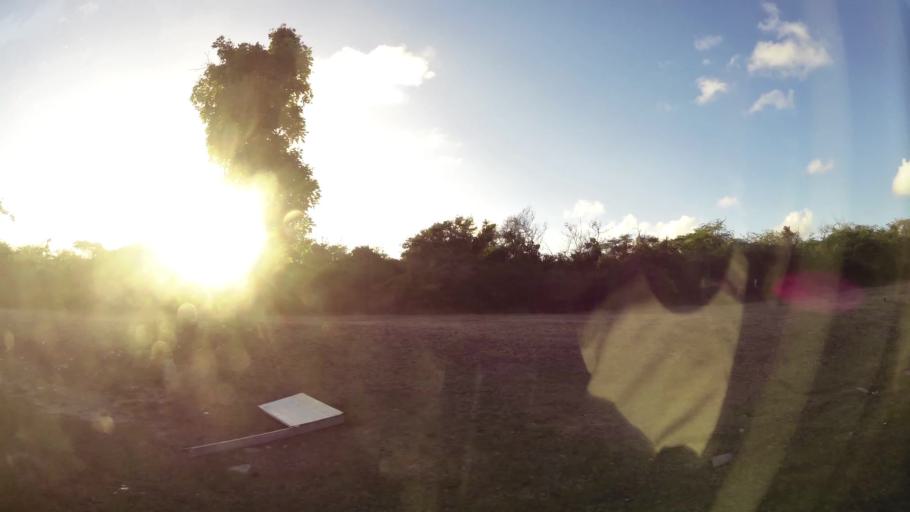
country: AG
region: Saint George
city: Piggotts
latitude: 17.1584
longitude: -61.7983
